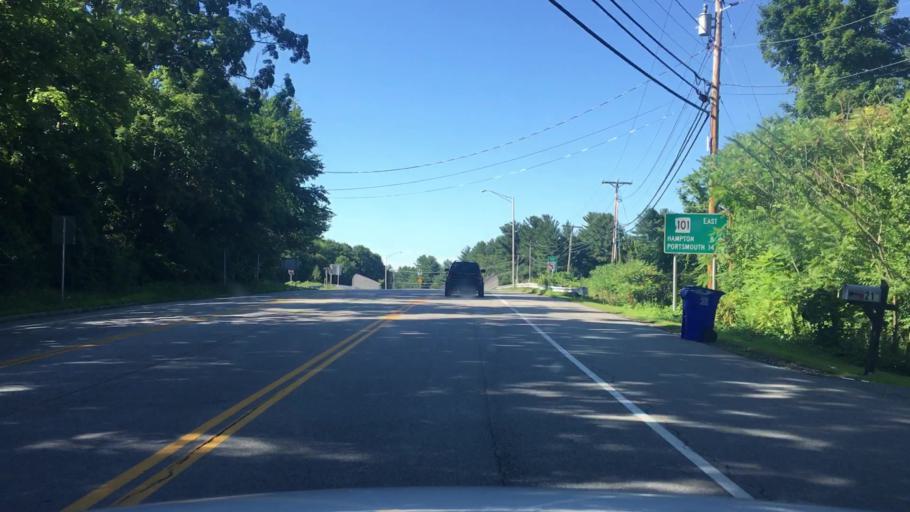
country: US
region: New Hampshire
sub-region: Rockingham County
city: Exeter
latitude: 42.9999
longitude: -70.9469
